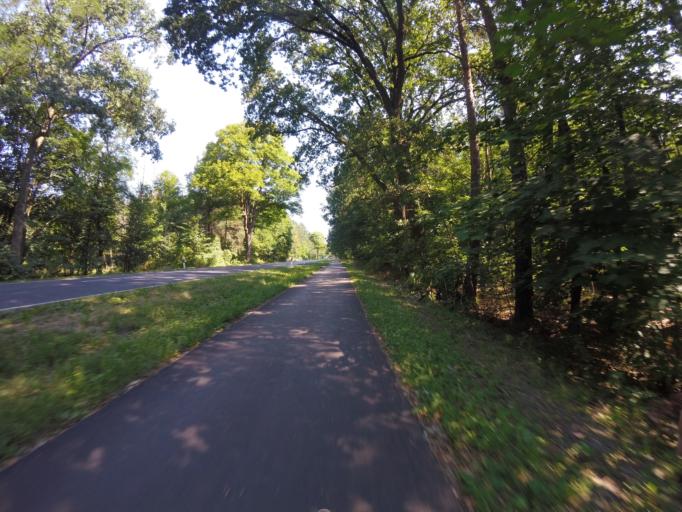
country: DE
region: Brandenburg
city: Mullrose
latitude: 52.2640
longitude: 14.4327
